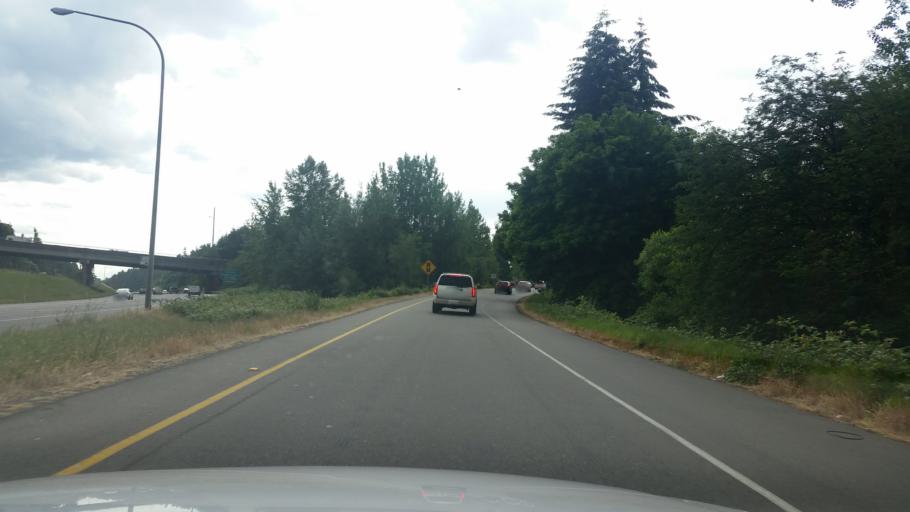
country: US
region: Washington
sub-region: Snohomish County
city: Mountlake Terrace
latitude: 47.8014
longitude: -122.3142
